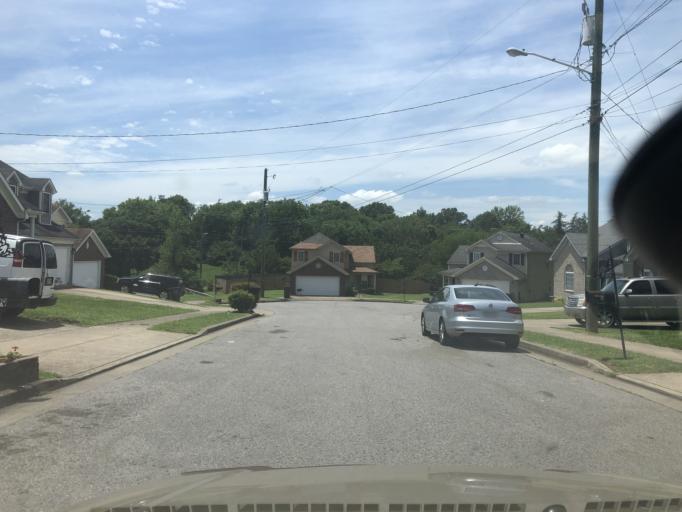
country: US
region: Tennessee
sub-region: Davidson County
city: Lakewood
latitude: 36.2470
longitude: -86.6797
